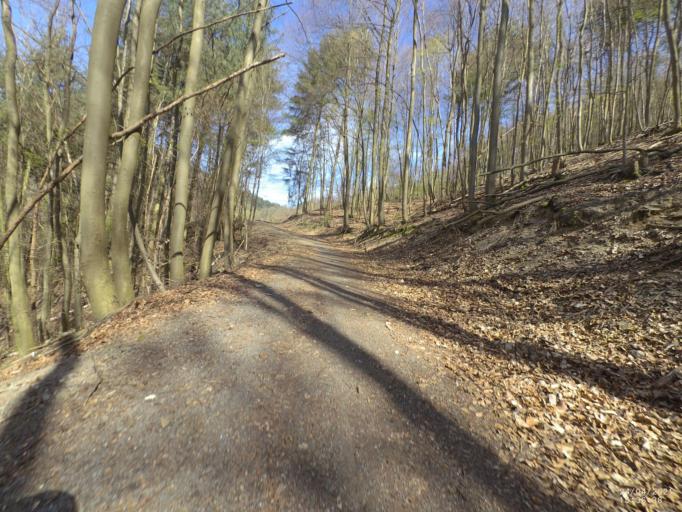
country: DE
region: Rheinland-Pfalz
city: Stromberg
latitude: 50.4541
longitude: 7.5843
